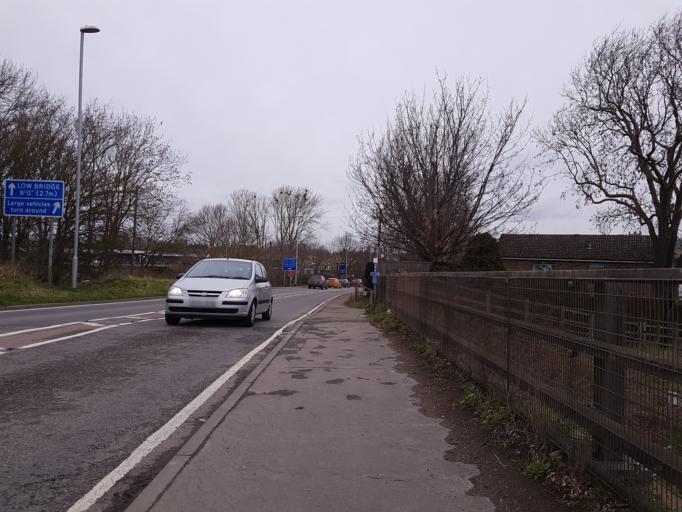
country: GB
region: England
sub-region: Cambridgeshire
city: Ely
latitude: 52.3902
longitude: 0.2691
